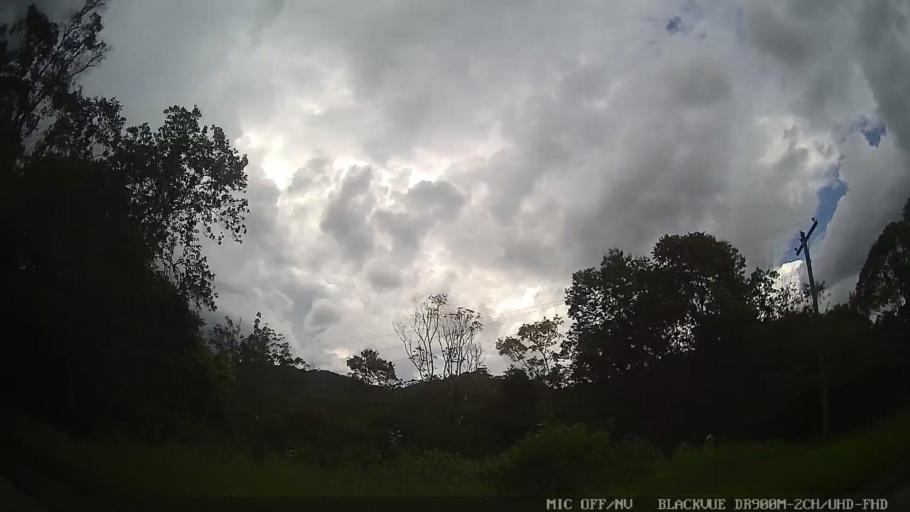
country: BR
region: Sao Paulo
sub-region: Caraguatatuba
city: Caraguatatuba
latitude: -23.5535
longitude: -45.6241
